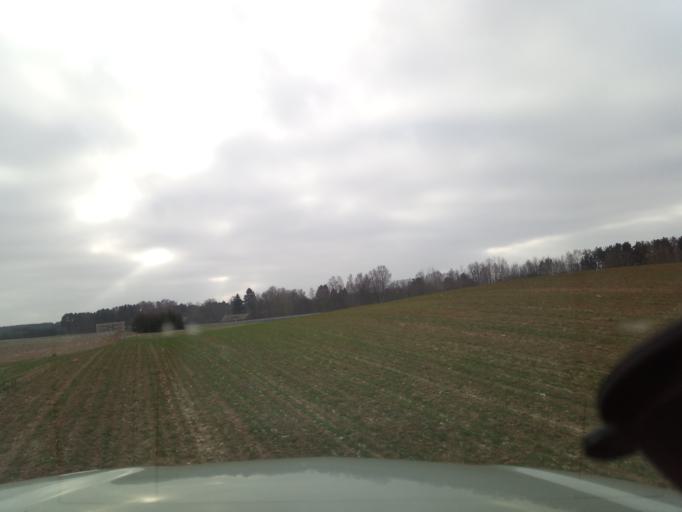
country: LT
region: Alytaus apskritis
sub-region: Alytaus rajonas
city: Daugai
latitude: 54.3173
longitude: 24.3697
